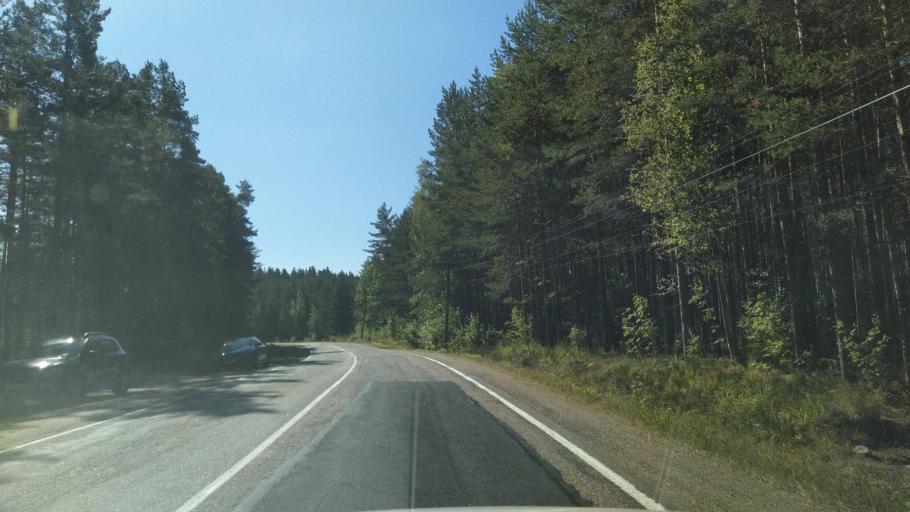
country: RU
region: Leningrad
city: Priozersk
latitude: 60.9810
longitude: 30.2695
